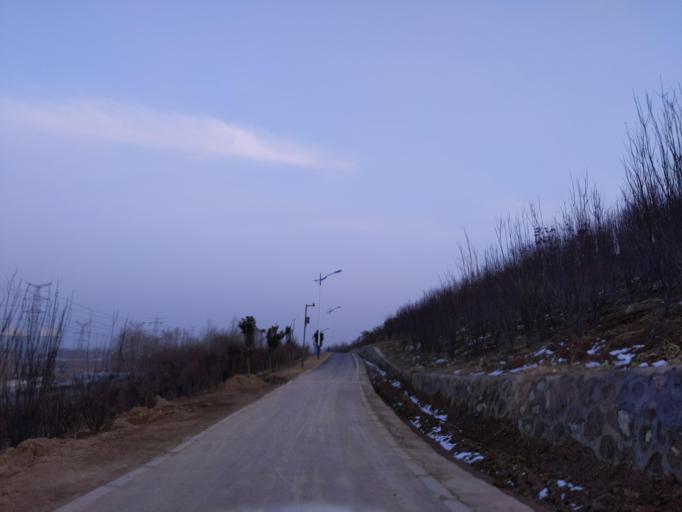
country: CN
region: Henan Sheng
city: Zhongyuanlu
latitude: 35.8165
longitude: 115.0566
